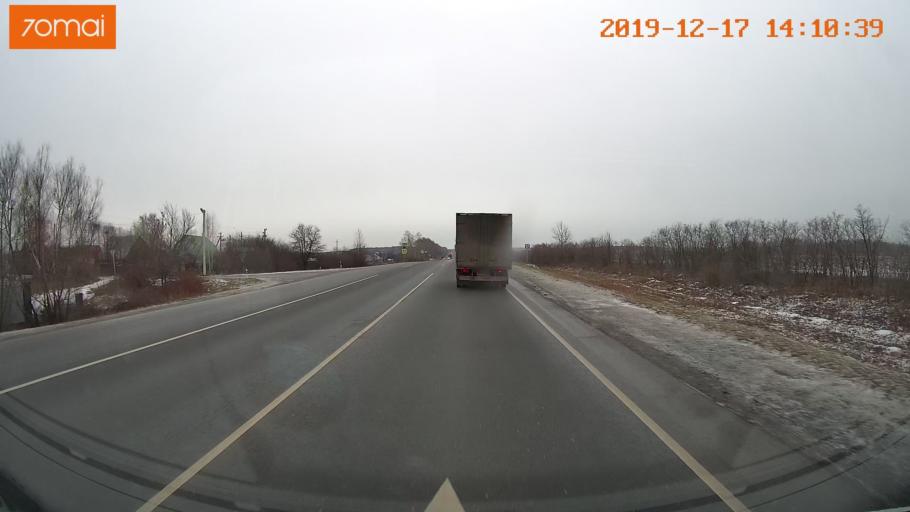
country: RU
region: Rjazan
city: Rybnoye
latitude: 54.5460
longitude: 39.5169
